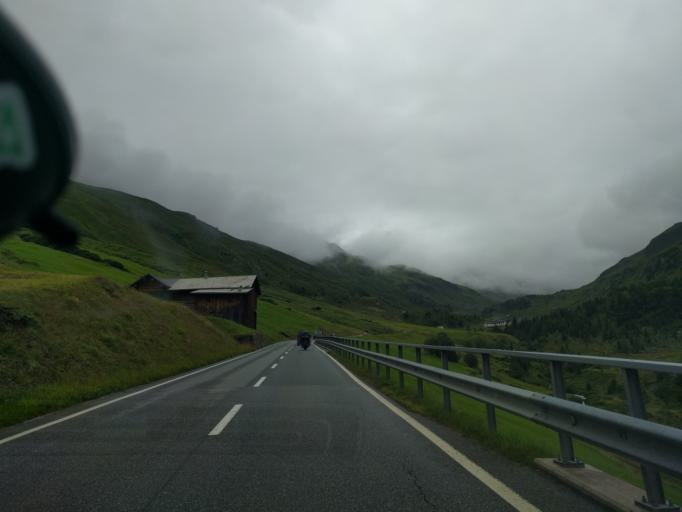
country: CH
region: Grisons
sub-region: Praettigau/Davos District
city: Davos
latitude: 46.7931
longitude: 9.9114
